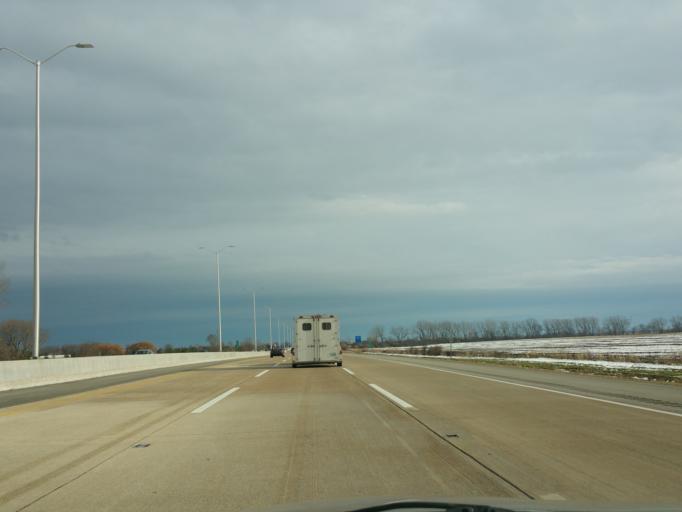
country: US
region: Illinois
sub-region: Boone County
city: Belvidere
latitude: 42.2188
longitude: -88.7471
